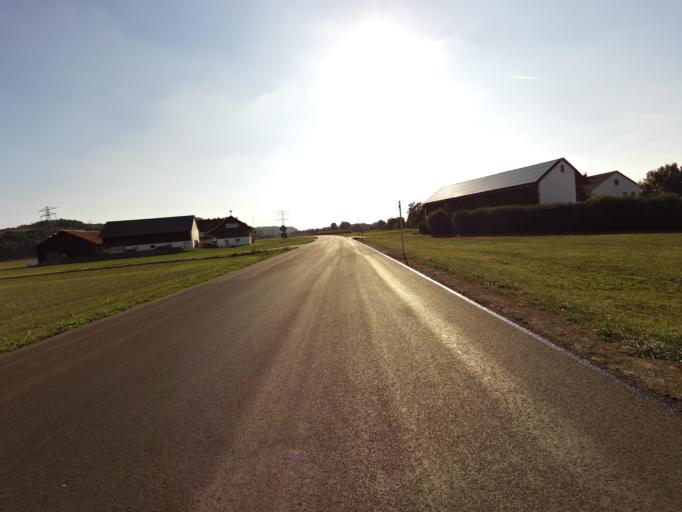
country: DE
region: Bavaria
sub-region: Lower Bavaria
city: Stallwang
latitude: 48.5846
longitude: 12.2473
